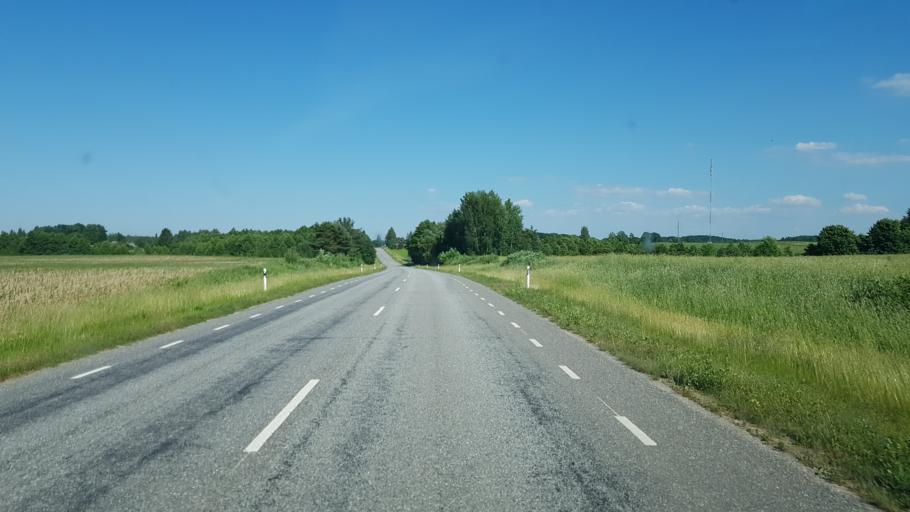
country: EE
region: Vorumaa
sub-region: Voru linn
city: Voru
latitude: 57.8554
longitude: 27.1681
